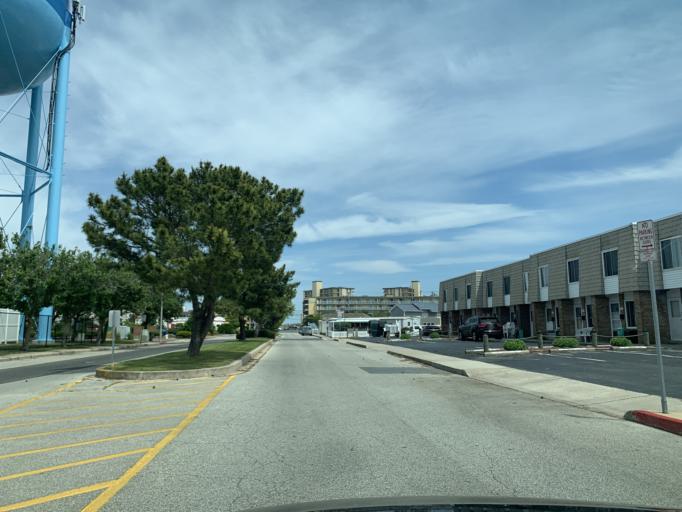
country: US
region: Delaware
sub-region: Sussex County
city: Bethany Beach
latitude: 38.4417
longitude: -75.0558
